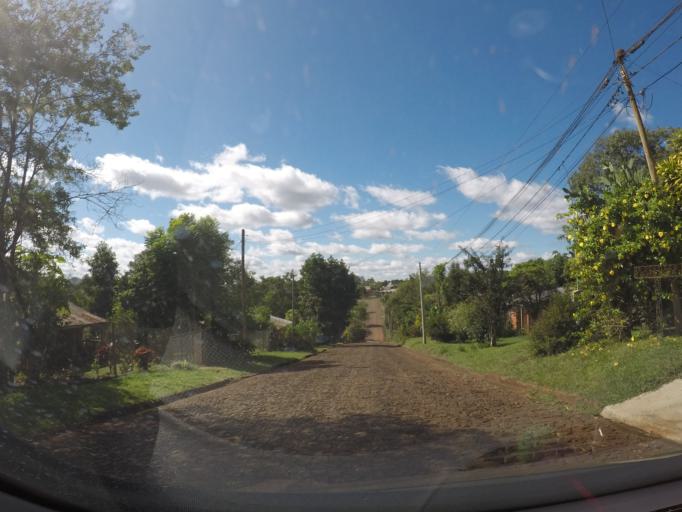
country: AR
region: Misiones
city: Puerto Rico
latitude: -26.7974
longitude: -55.0164
